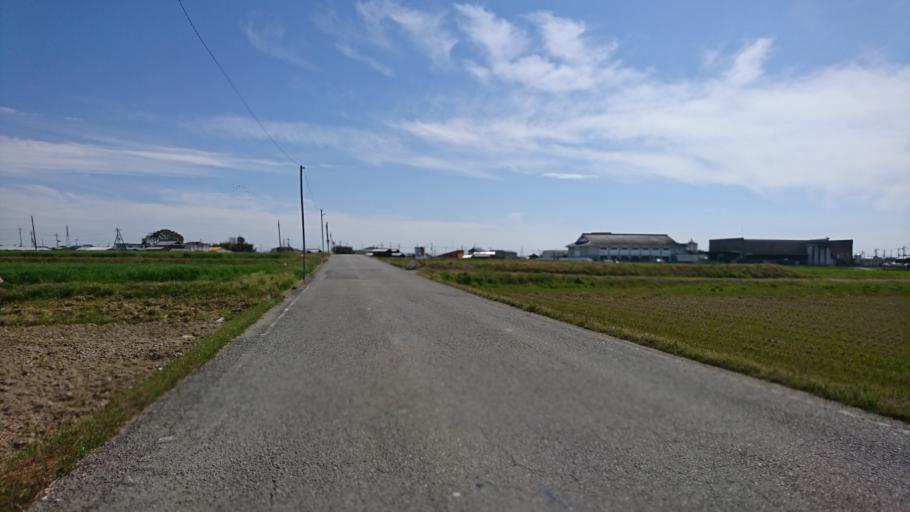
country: JP
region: Hyogo
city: Miki
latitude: 34.7570
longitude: 134.9345
